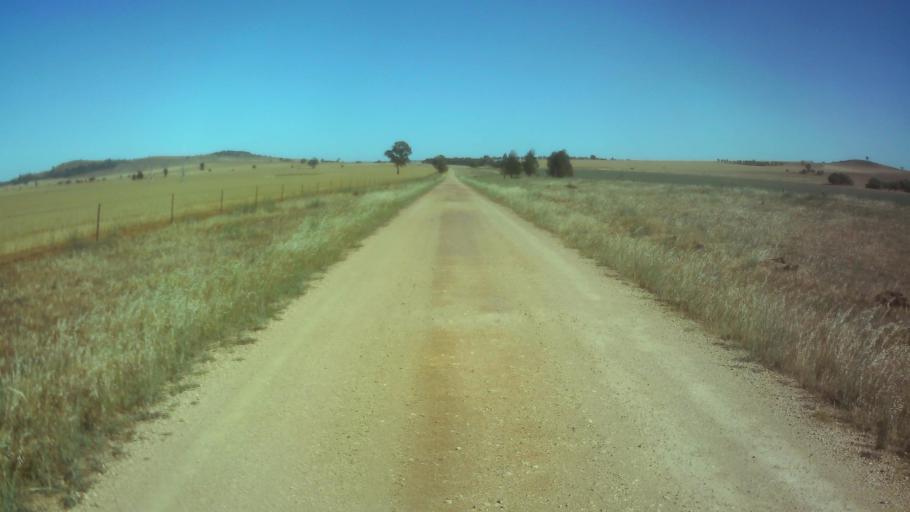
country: AU
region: New South Wales
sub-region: Weddin
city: Grenfell
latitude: -33.9768
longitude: 148.3240
